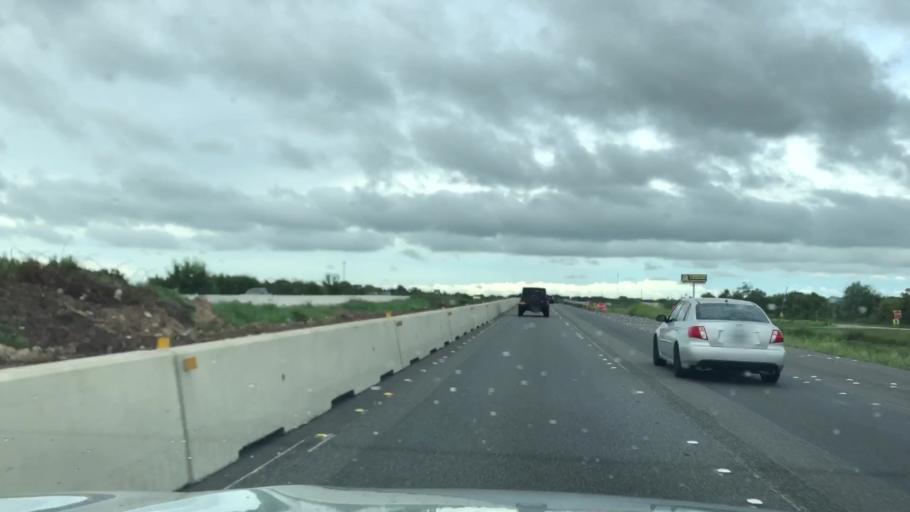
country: US
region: Texas
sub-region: Waller County
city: Brookshire
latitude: 29.7783
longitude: -96.0060
